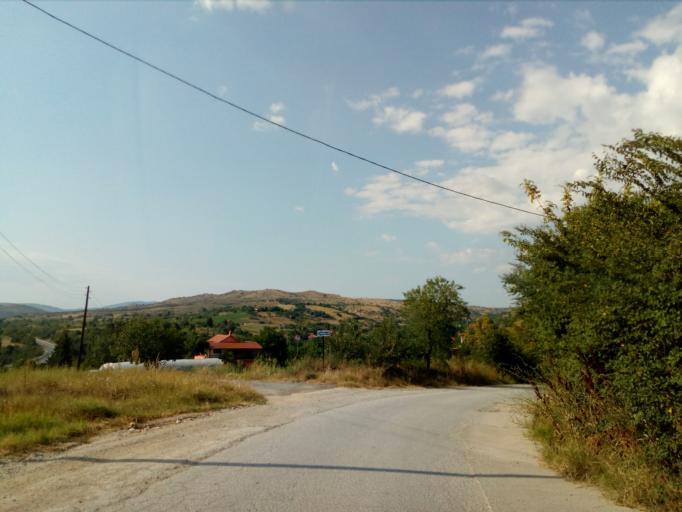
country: MK
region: Veles
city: Veles
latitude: 41.7352
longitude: 21.7888
